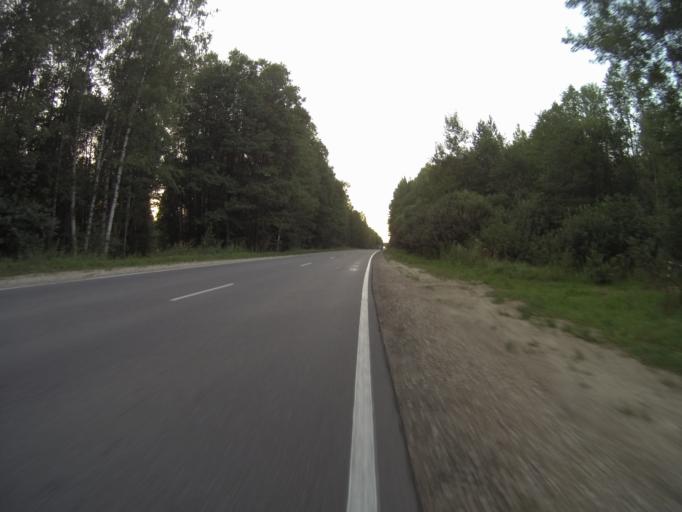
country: RU
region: Vladimir
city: Anopino
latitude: 55.8613
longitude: 40.6363
